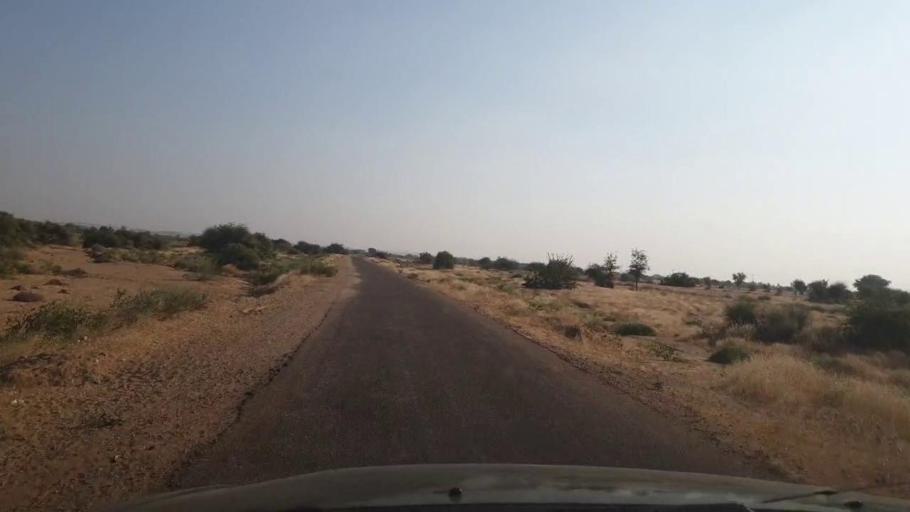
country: PK
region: Sindh
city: Jamshoro
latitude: 25.3456
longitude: 67.8384
